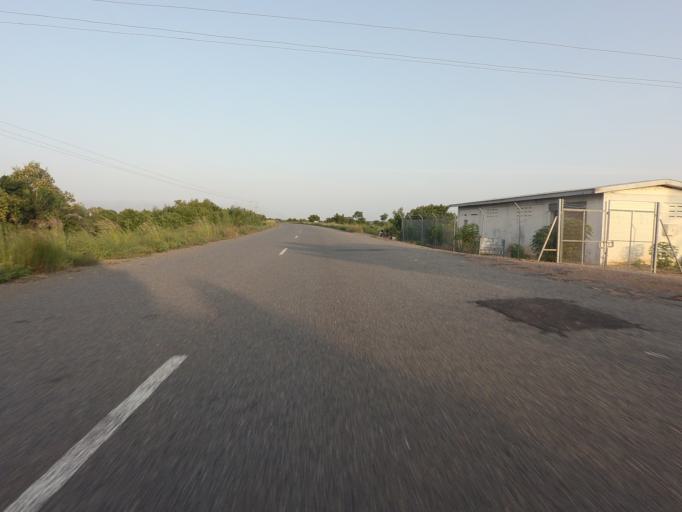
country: GH
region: Volta
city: Anloga
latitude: 5.8565
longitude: 0.7669
